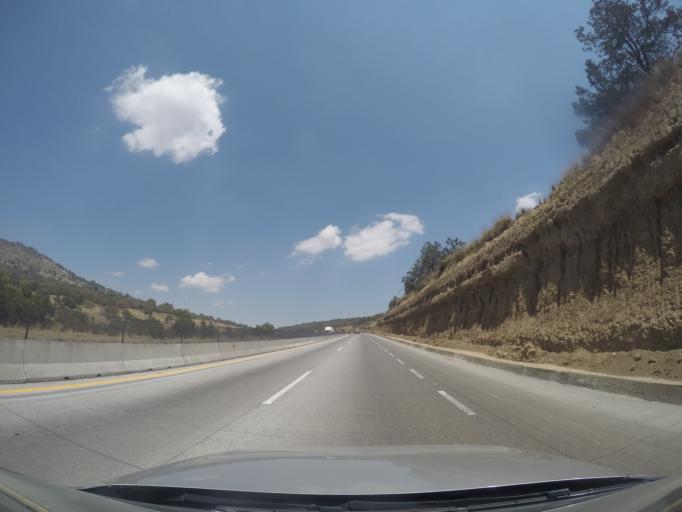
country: MX
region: Tlaxcala
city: Espanita
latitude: 19.4674
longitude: -98.4516
